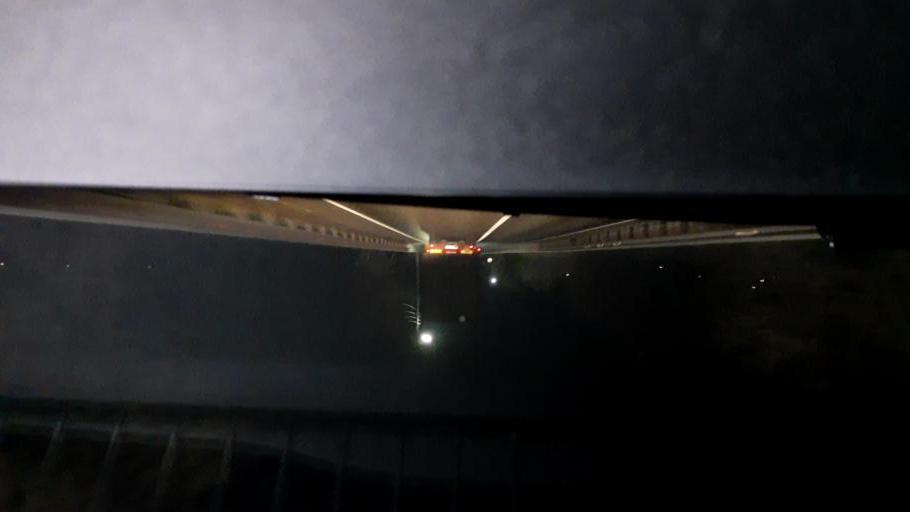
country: RU
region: Nizjnij Novgorod
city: Gidrotorf
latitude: 56.5316
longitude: 43.5430
